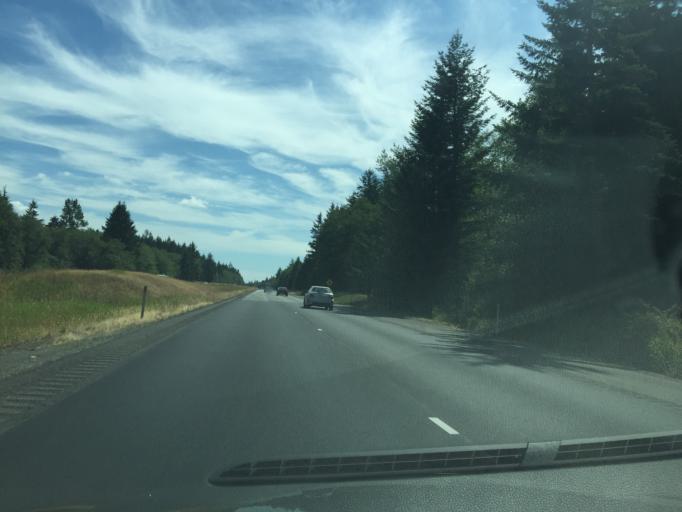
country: US
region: Washington
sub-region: Skagit County
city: Burlington
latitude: 48.5856
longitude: -122.3454
